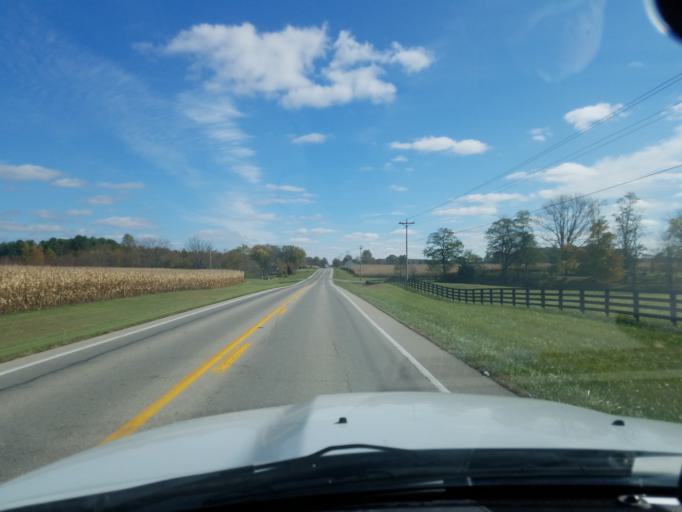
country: US
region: Indiana
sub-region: Ripley County
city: Osgood
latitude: 39.0750
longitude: -85.3174
